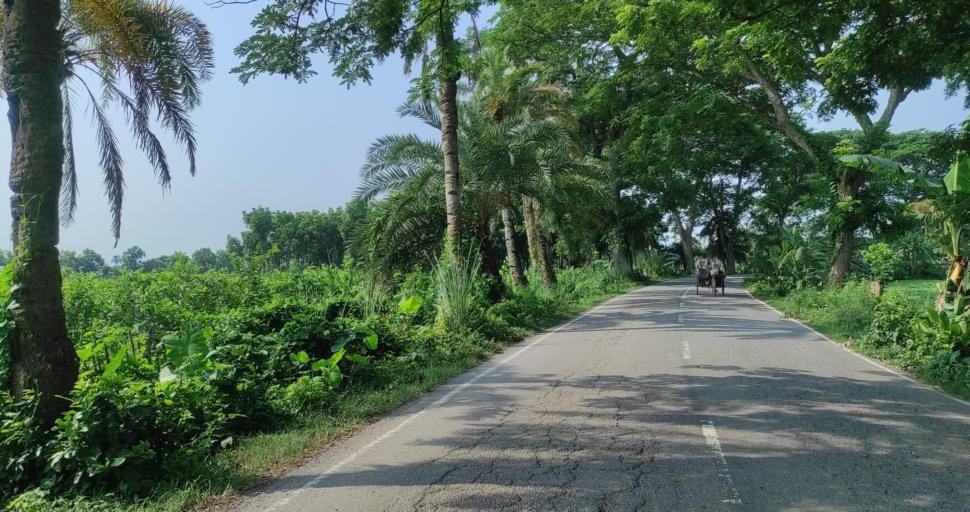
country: BD
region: Rajshahi
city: Ishurdi
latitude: 24.2803
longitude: 89.0643
